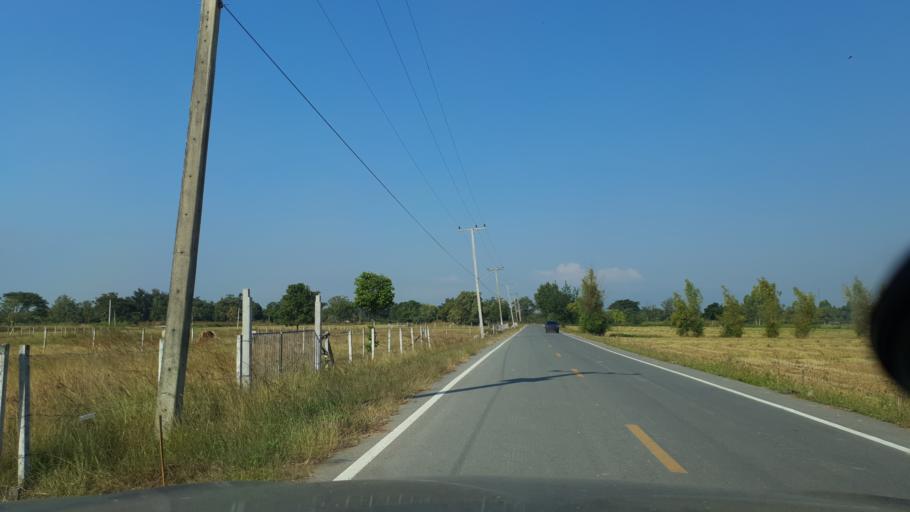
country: TH
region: Lamphun
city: Ban Thi
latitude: 18.6839
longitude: 99.1180
